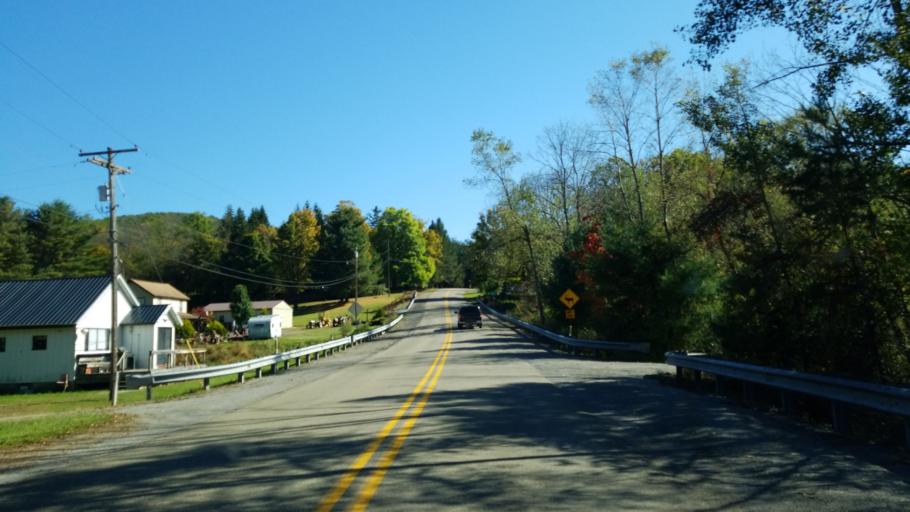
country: US
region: Pennsylvania
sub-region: Elk County
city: Saint Marys
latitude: 41.2889
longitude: -78.3965
